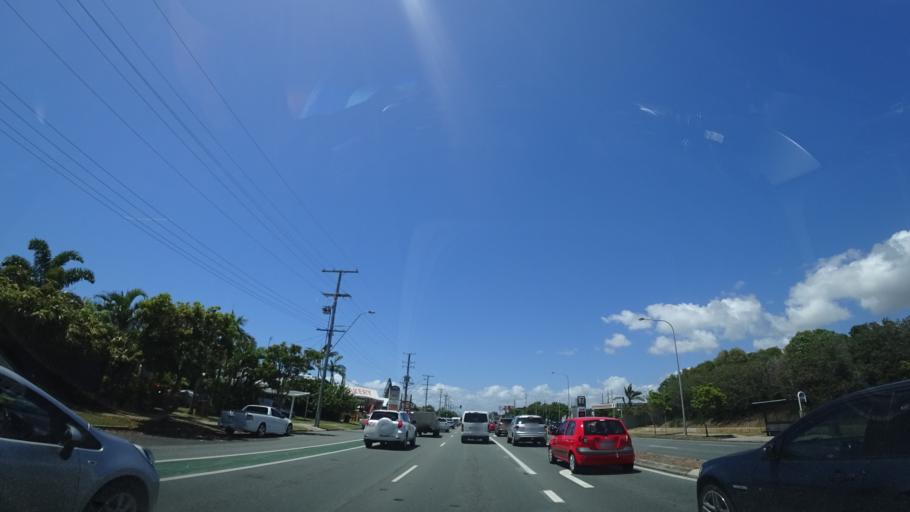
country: AU
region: Queensland
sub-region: Sunshine Coast
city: Mooloolaba
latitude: -26.7179
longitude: 153.1298
